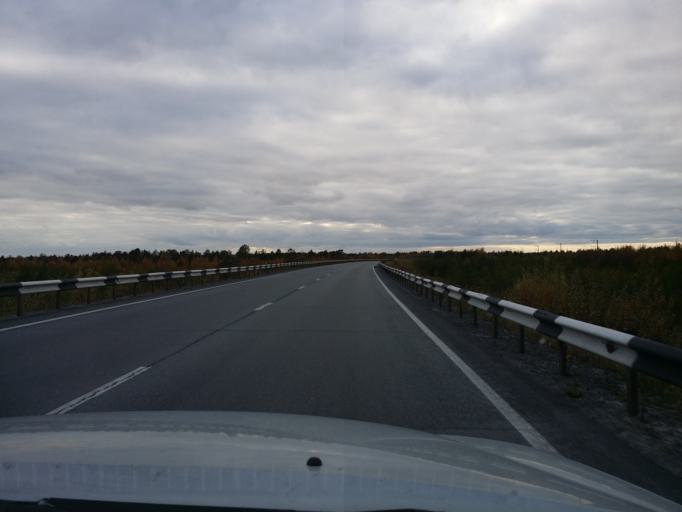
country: RU
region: Khanty-Mansiyskiy Avtonomnyy Okrug
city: Lokosovo
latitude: 61.4455
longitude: 74.5741
